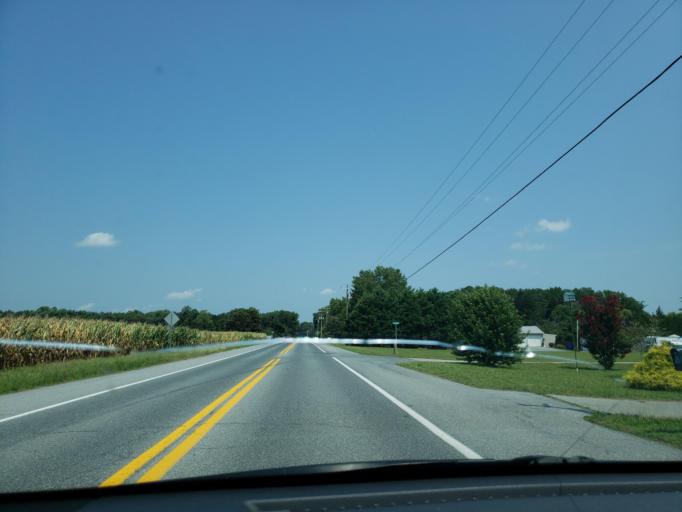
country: US
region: Delaware
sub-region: Sussex County
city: Milton
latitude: 38.8146
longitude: -75.3095
